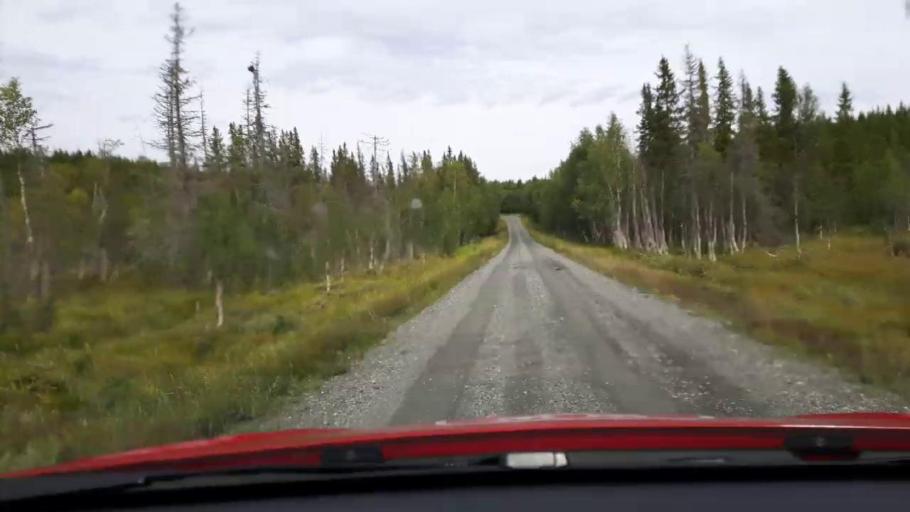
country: SE
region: Jaemtland
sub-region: Are Kommun
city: Are
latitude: 63.7819
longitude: 13.1018
